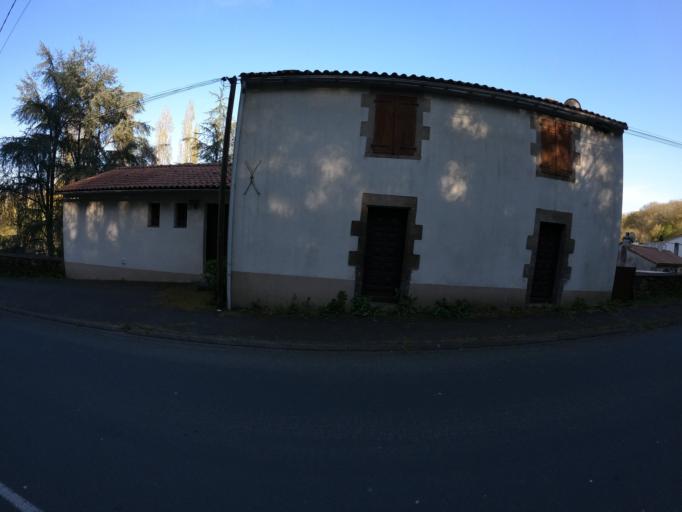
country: FR
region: Pays de la Loire
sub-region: Departement de la Vendee
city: Mortagne-sur-Sevre
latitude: 46.9863
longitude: -0.9610
